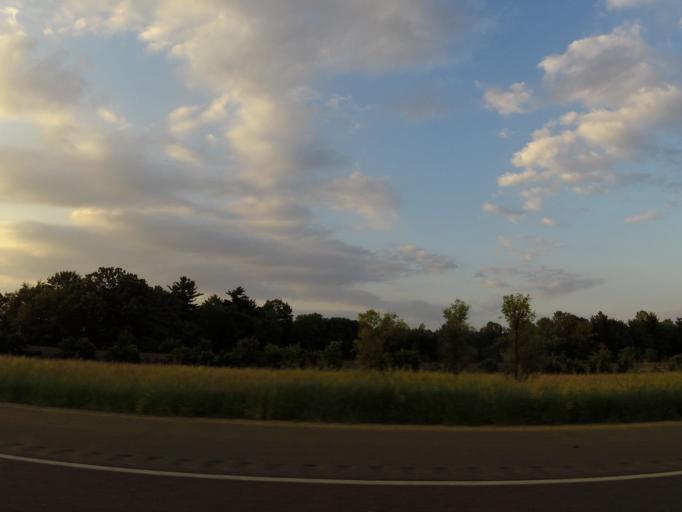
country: US
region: Wisconsin
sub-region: Dunn County
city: Colfax
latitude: 44.8993
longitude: -91.7581
